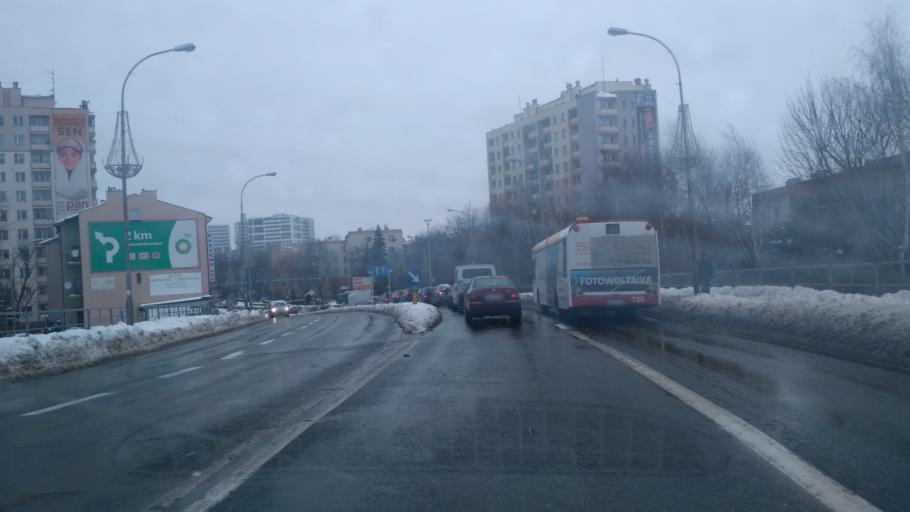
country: PL
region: Subcarpathian Voivodeship
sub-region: Rzeszow
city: Rzeszow
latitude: 50.0439
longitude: 22.0002
